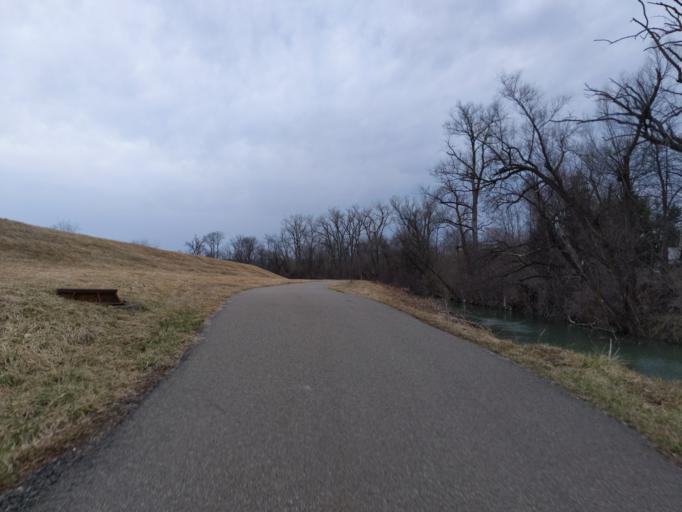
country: US
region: New York
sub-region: Chemung County
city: Elmira
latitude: 42.0965
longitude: -76.7891
